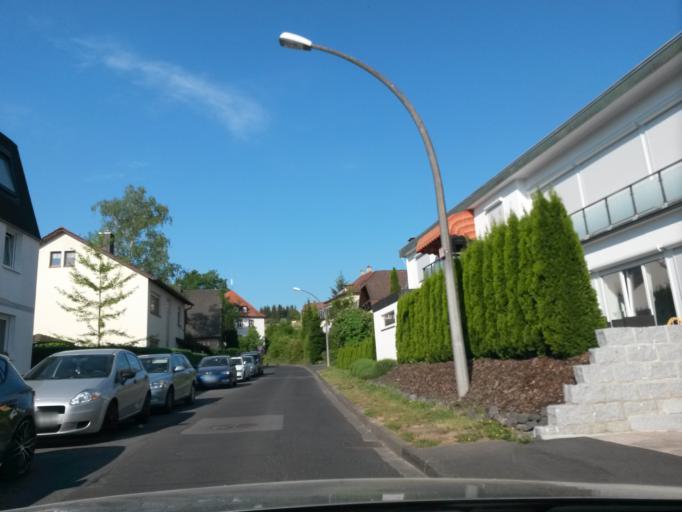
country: DE
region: Bavaria
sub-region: Regierungsbezirk Unterfranken
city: Bad Kissingen
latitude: 50.1974
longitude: 10.0617
